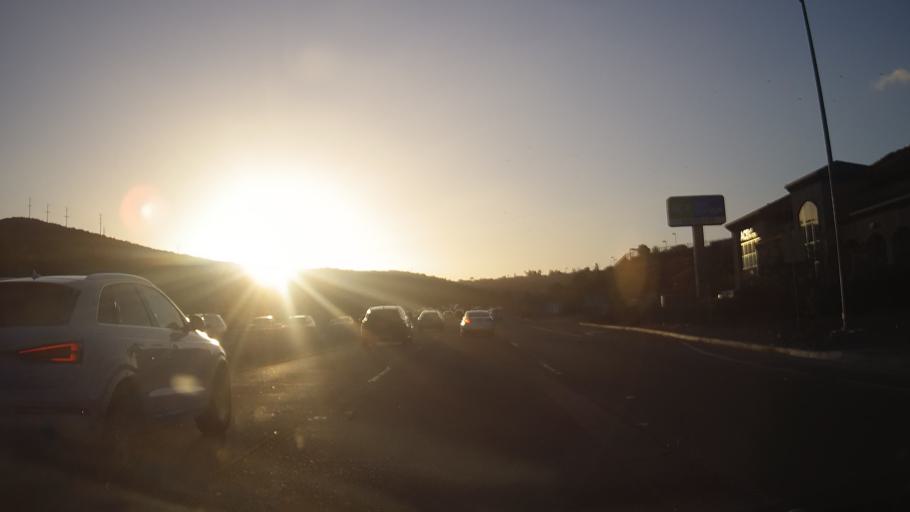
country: US
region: California
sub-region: San Diego County
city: Rancho San Diego
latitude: 32.7392
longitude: -116.9449
